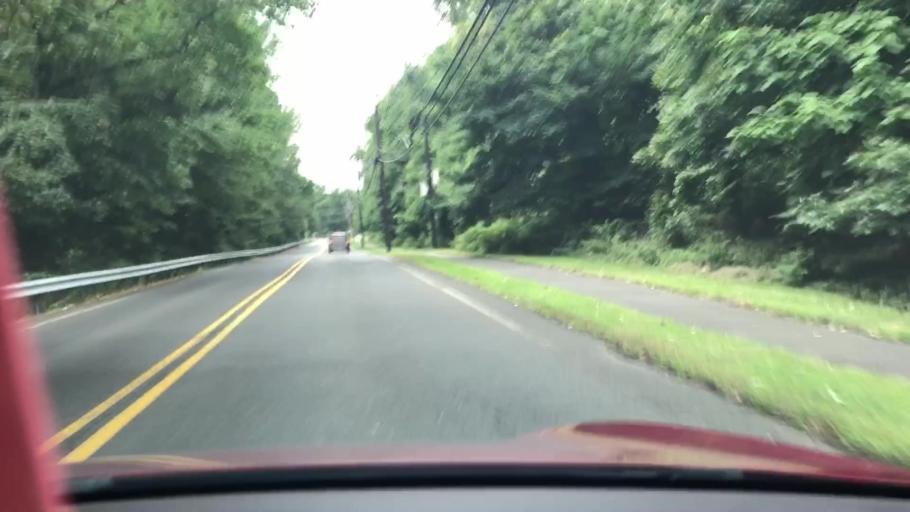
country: US
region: New Jersey
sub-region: Mercer County
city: Yardville
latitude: 40.1902
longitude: -74.6407
